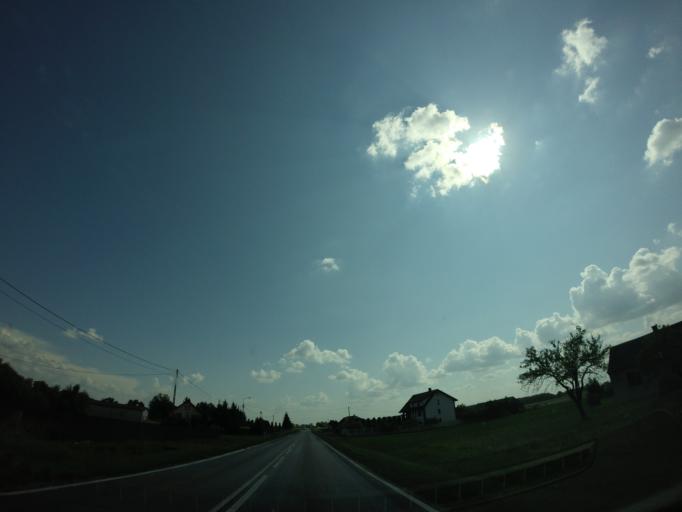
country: PL
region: Podlasie
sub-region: Powiat zambrowski
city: Zambrow
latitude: 52.9102
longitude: 22.2549
